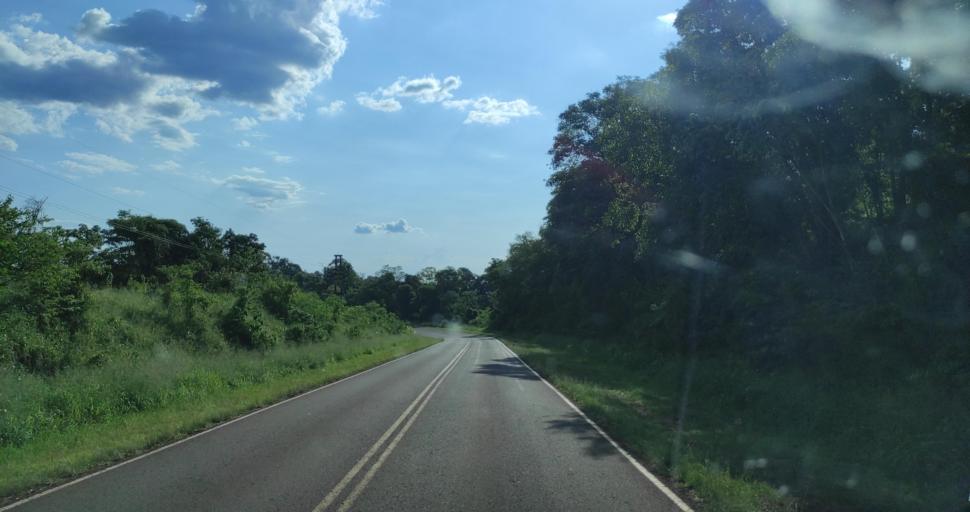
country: AR
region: Misiones
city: San Vicente
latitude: -26.3506
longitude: -54.2076
